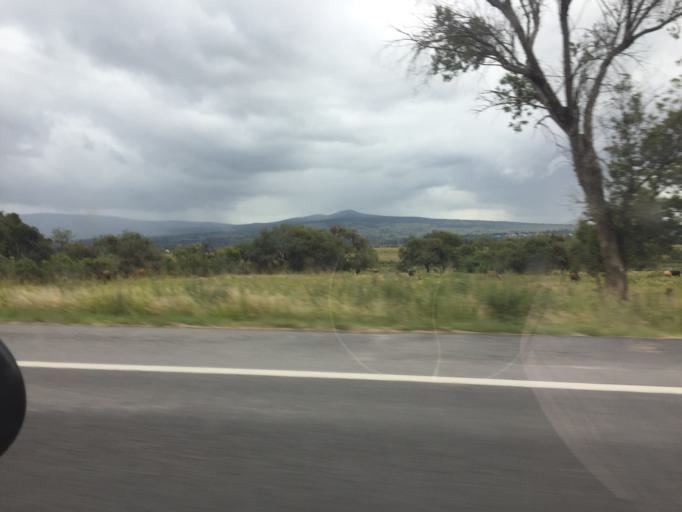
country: MX
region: Jalisco
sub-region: Zapotlanejo
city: La Mezquitera
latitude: 20.5680
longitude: -103.0800
